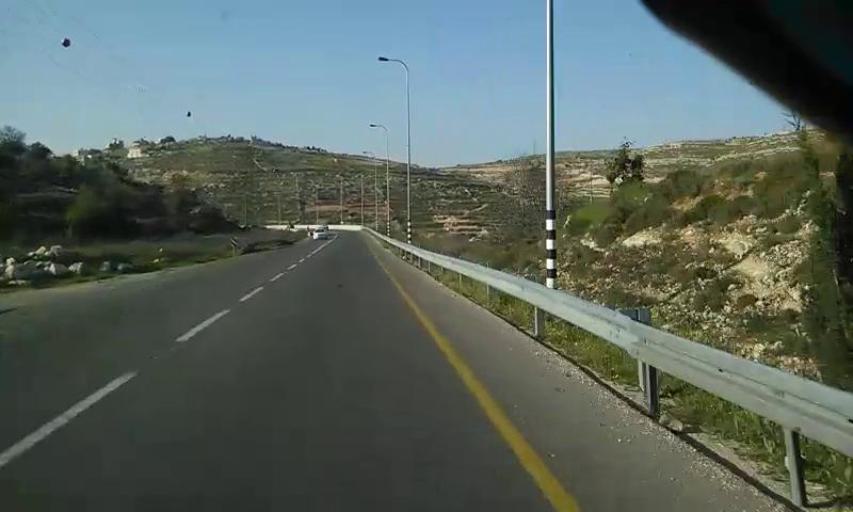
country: PS
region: West Bank
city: Halhul
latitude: 31.5936
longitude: 35.1151
